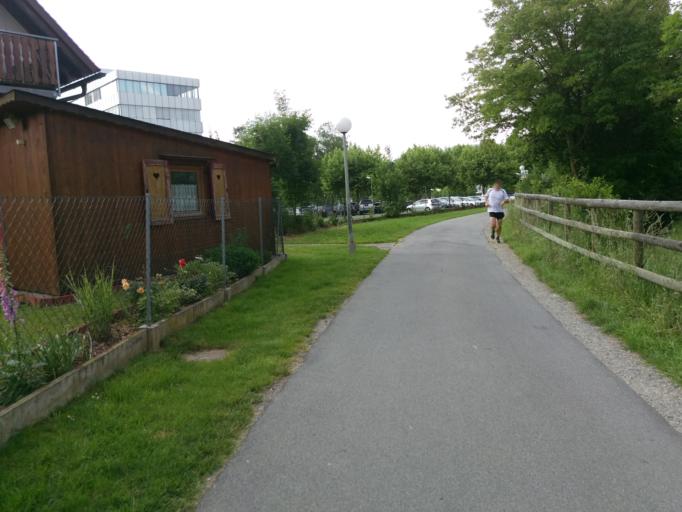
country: AT
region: Styria
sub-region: Politischer Bezirk Graz-Umgebung
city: Stattegg
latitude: 47.1078
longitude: 15.4250
